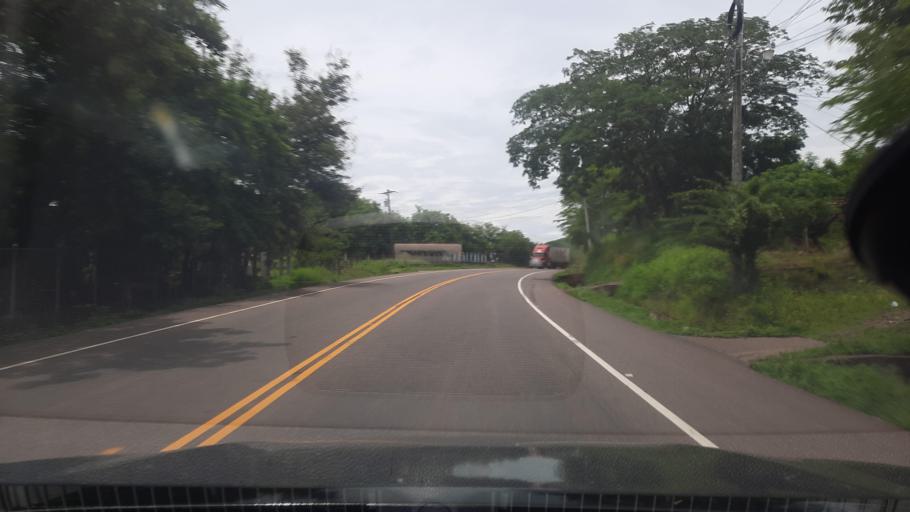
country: HN
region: Valle
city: Langue
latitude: 13.5788
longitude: -87.6821
